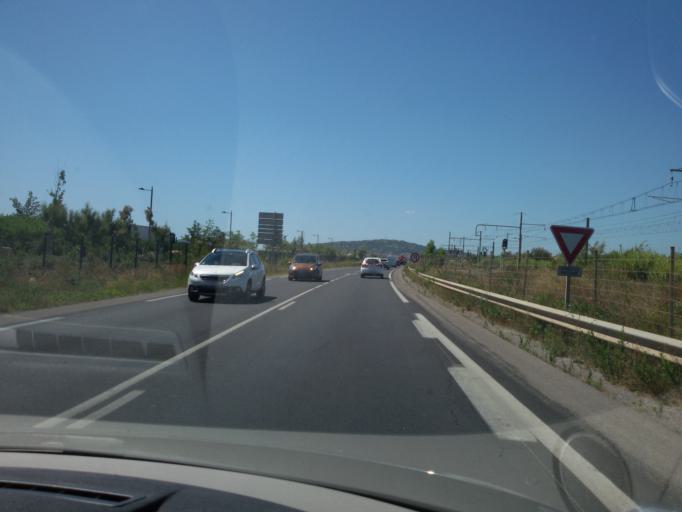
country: FR
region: Languedoc-Roussillon
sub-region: Departement de l'Herault
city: Frontignan
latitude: 43.4241
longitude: 3.7458
